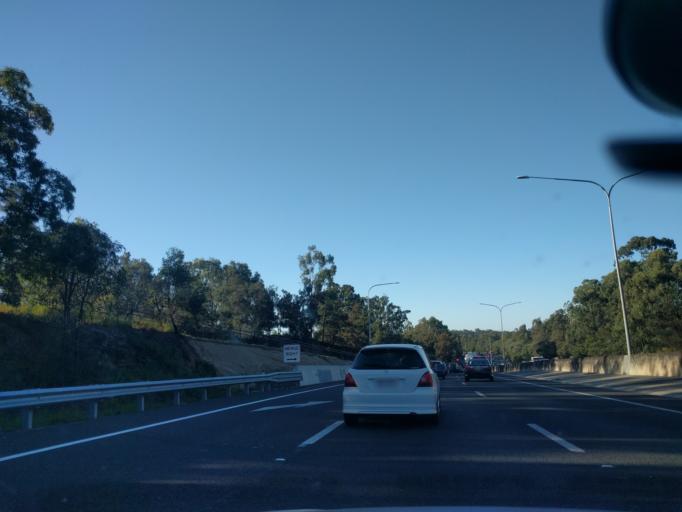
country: AU
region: Queensland
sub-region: Brisbane
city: Seventeen Mile Rocks
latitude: -27.5436
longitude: 152.9429
